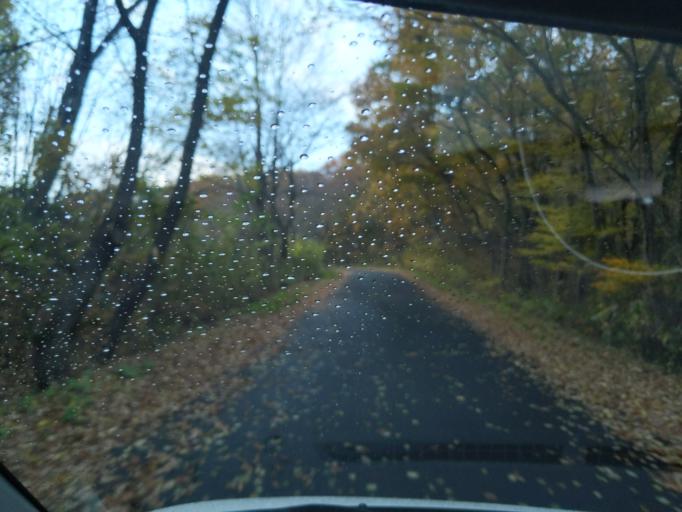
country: JP
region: Iwate
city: Mizusawa
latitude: 39.0753
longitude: 141.0289
